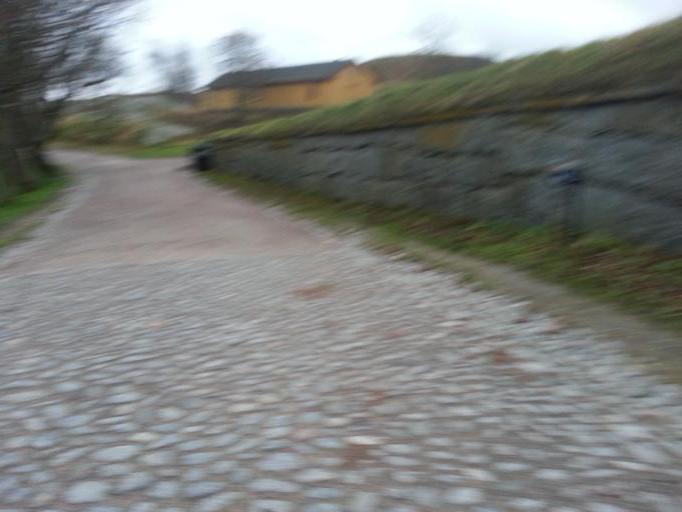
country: FI
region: Uusimaa
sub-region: Helsinki
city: Helsinki
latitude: 60.1414
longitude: 24.9853
